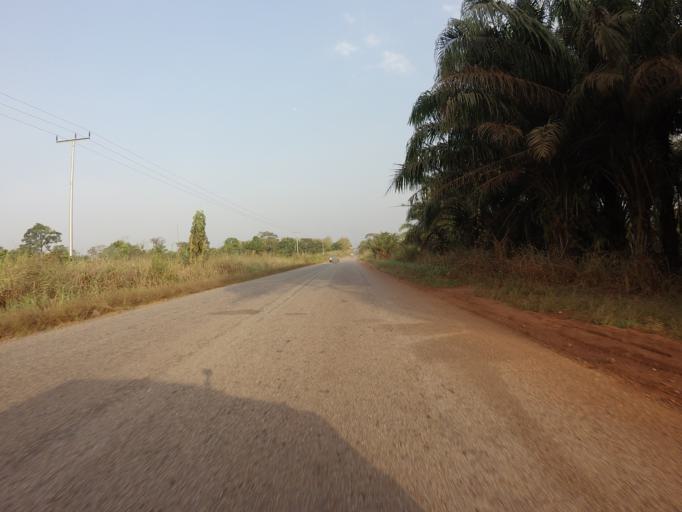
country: GH
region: Volta
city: Ho
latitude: 6.5749
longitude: 0.3181
